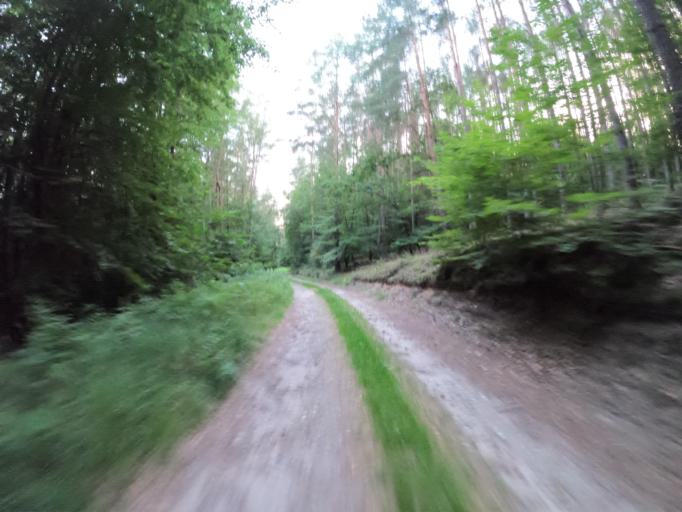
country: PL
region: West Pomeranian Voivodeship
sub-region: Powiat koszalinski
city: Sianow
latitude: 54.0838
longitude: 16.4026
